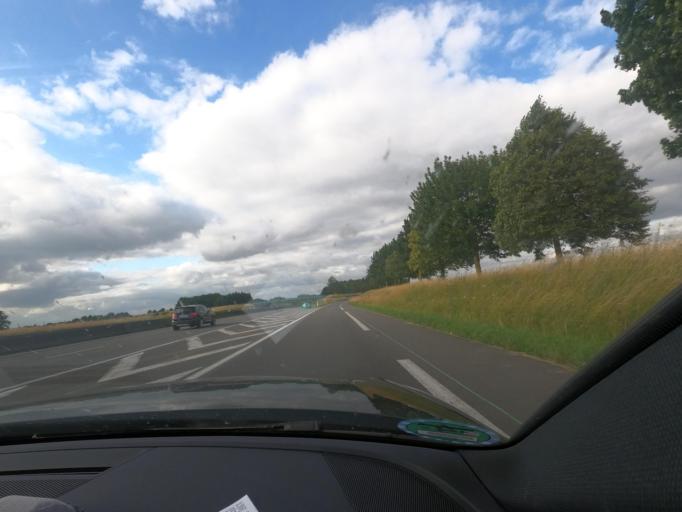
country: FR
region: Picardie
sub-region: Departement de la Somme
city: Pont-de-Metz
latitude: 49.8898
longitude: 2.2282
